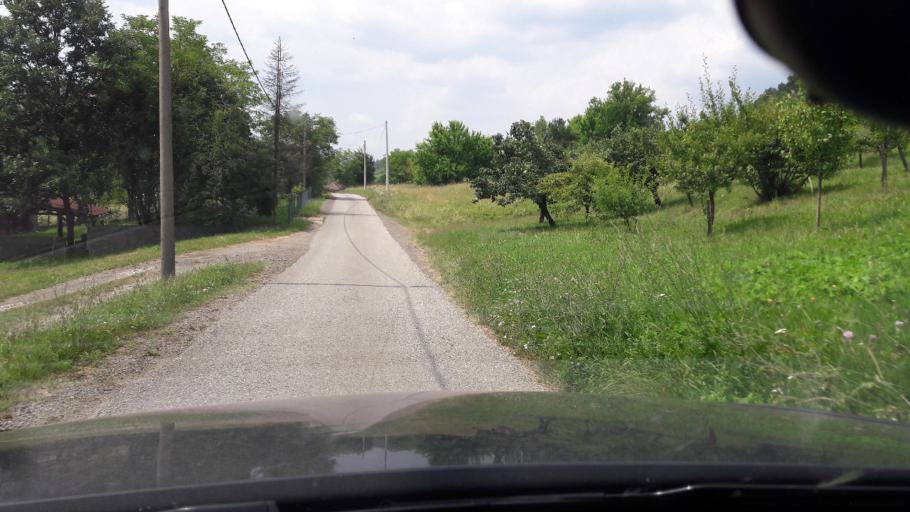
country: RS
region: Central Serbia
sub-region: Belgrade
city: Sopot
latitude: 44.6292
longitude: 20.5957
